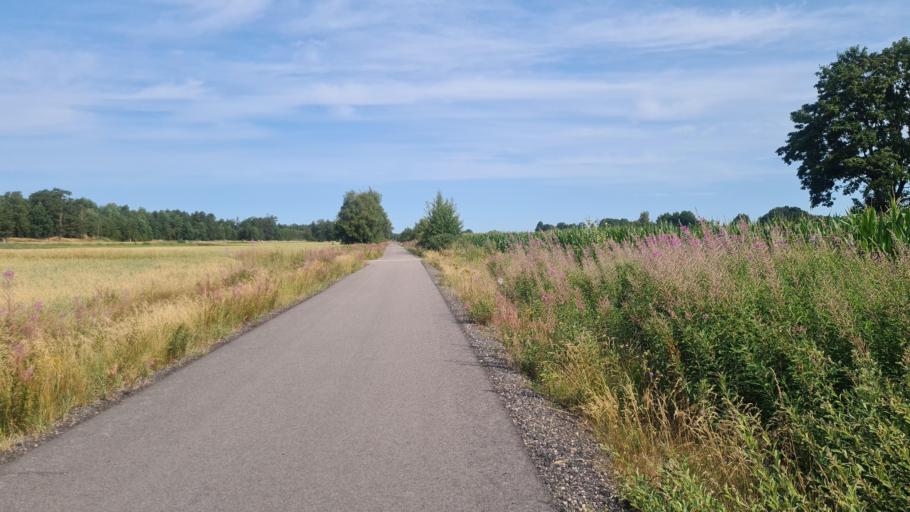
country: SE
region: Kronoberg
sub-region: Ljungby Kommun
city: Lagan
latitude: 56.8747
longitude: 13.9836
